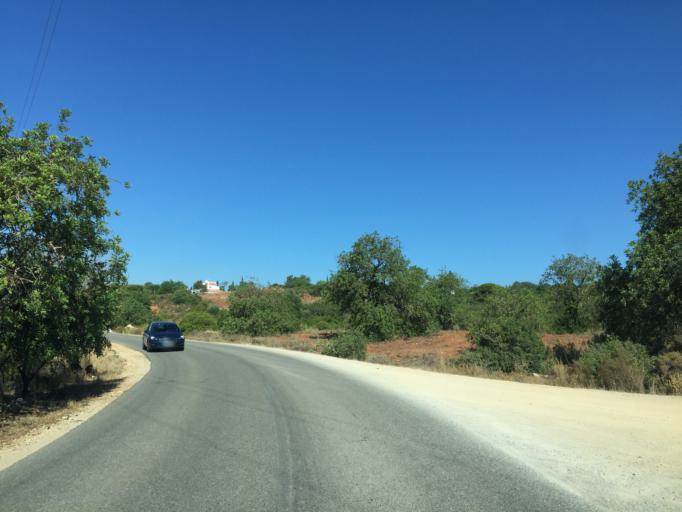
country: PT
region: Faro
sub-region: Loule
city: Vilamoura
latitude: 37.1159
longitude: -8.0772
